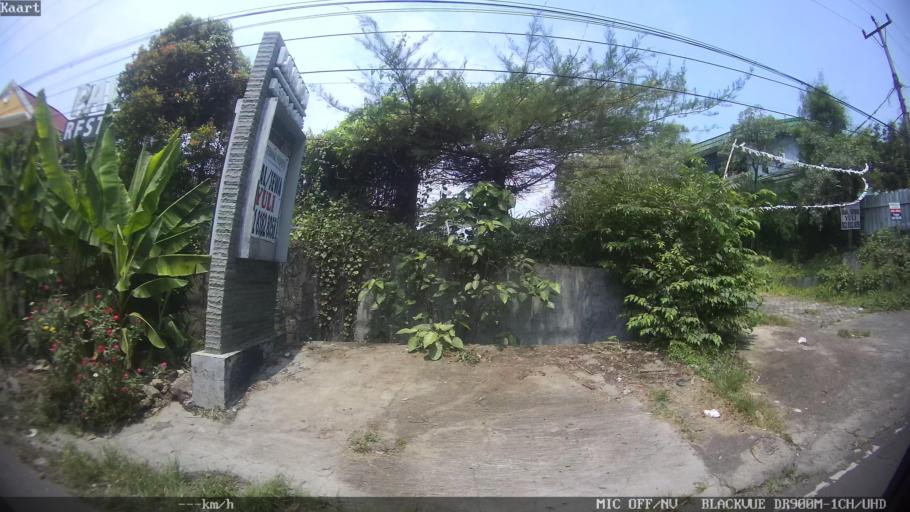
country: ID
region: Lampung
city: Bandarlampung
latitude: -5.4333
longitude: 105.2729
